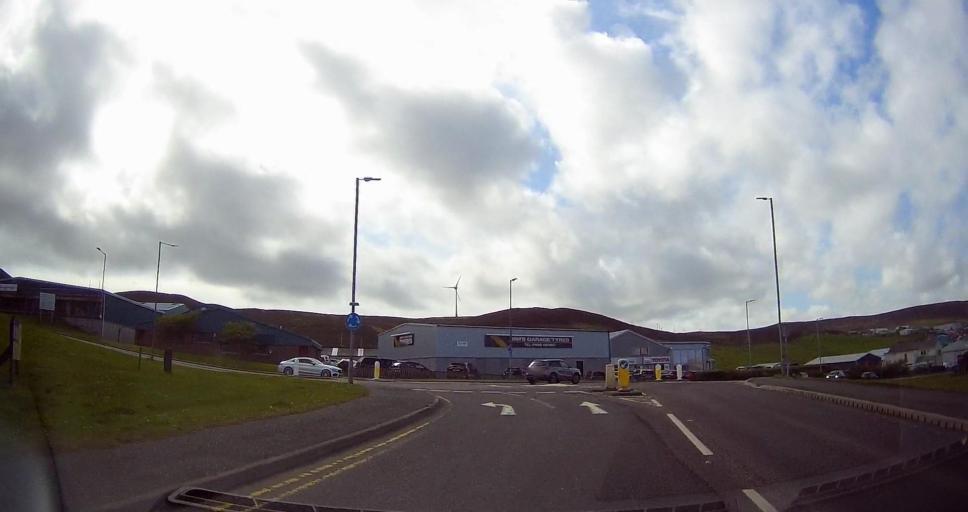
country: GB
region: Scotland
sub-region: Shetland Islands
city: Lerwick
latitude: 60.1647
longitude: -1.1642
